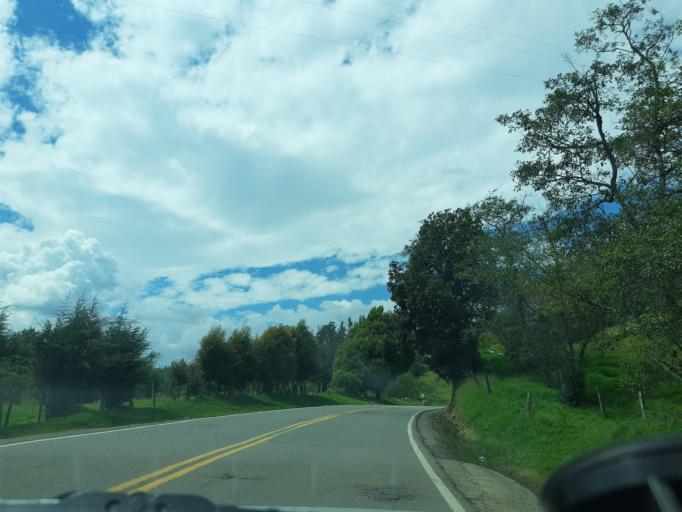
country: CO
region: Boyaca
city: Chiquinquira
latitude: 5.6223
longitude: -73.7521
